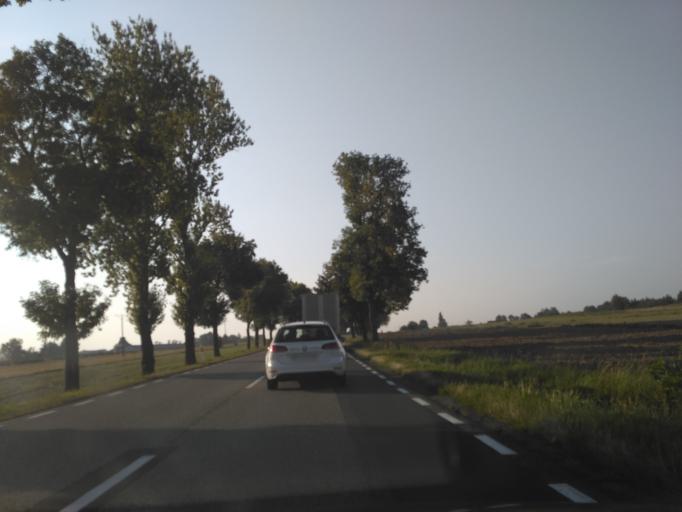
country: PL
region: Lublin Voivodeship
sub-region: Powiat krasnicki
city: Szastarka
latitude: 50.8370
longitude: 22.3022
